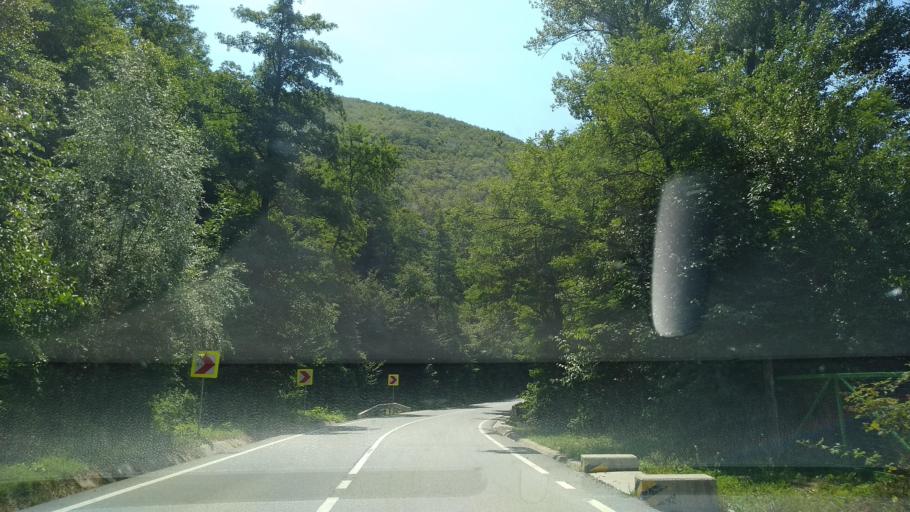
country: RO
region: Gorj
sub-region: Comuna Bumbesti-Jiu
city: Bumbesti-Jiu
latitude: 45.2131
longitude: 23.3794
